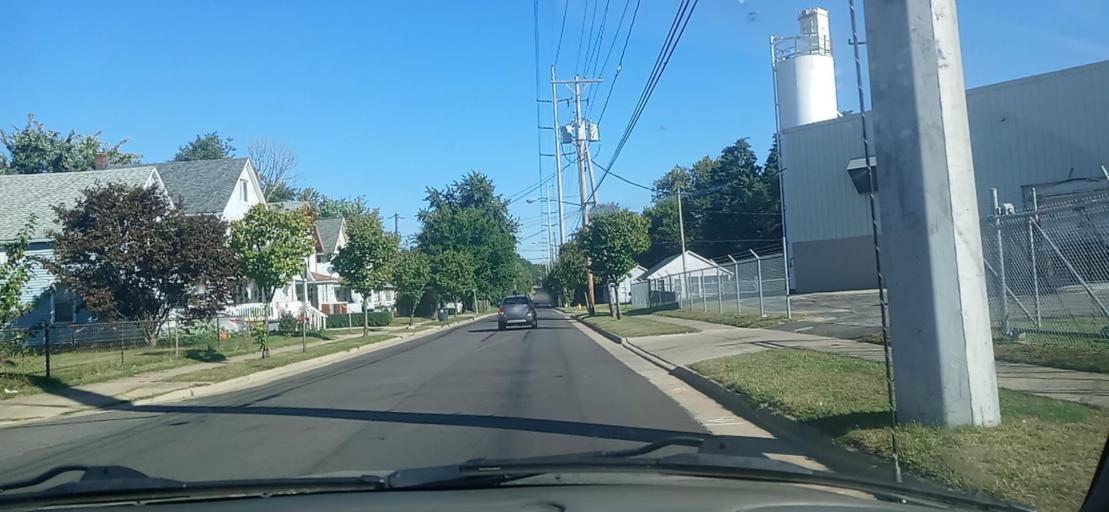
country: US
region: Ohio
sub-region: Summit County
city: Akron
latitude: 41.0510
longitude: -81.5414
